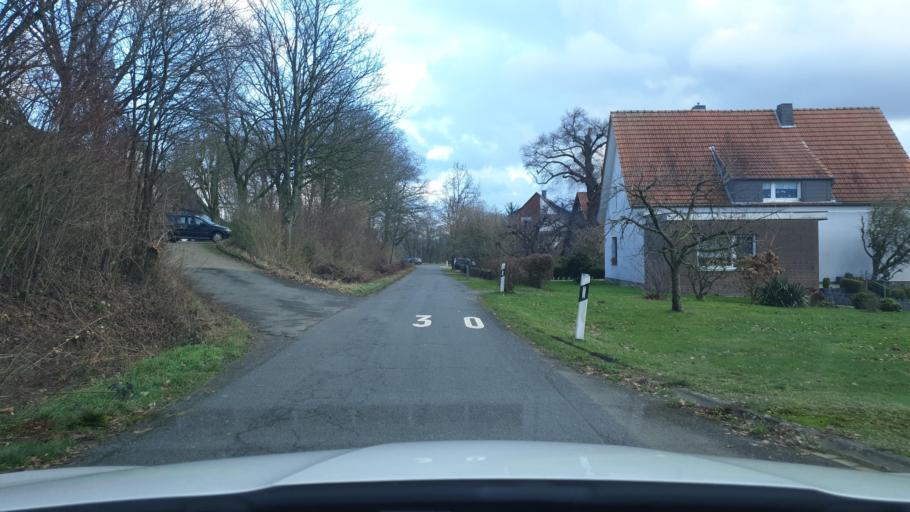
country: DE
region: North Rhine-Westphalia
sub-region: Regierungsbezirk Detmold
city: Bad Salzuflen
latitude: 52.1400
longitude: 8.7782
